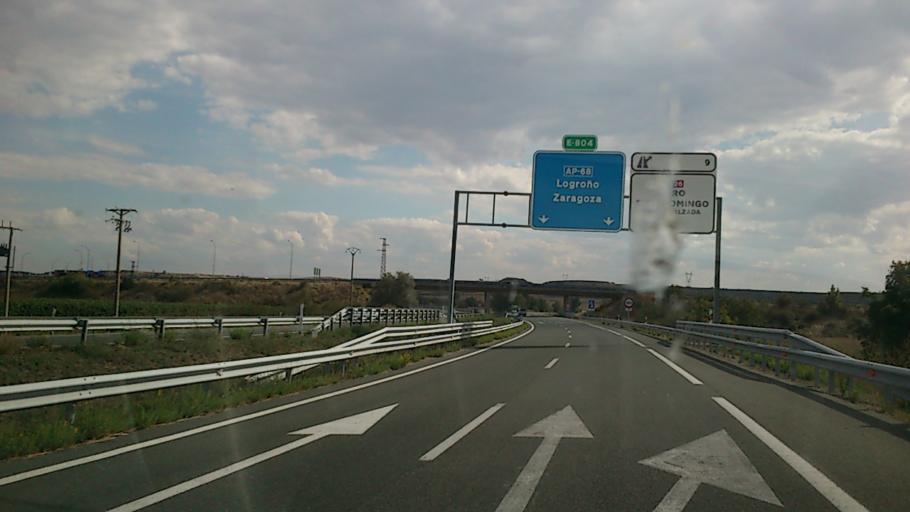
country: ES
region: La Rioja
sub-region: Provincia de La Rioja
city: Anguciana
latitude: 42.5641
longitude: -2.8798
